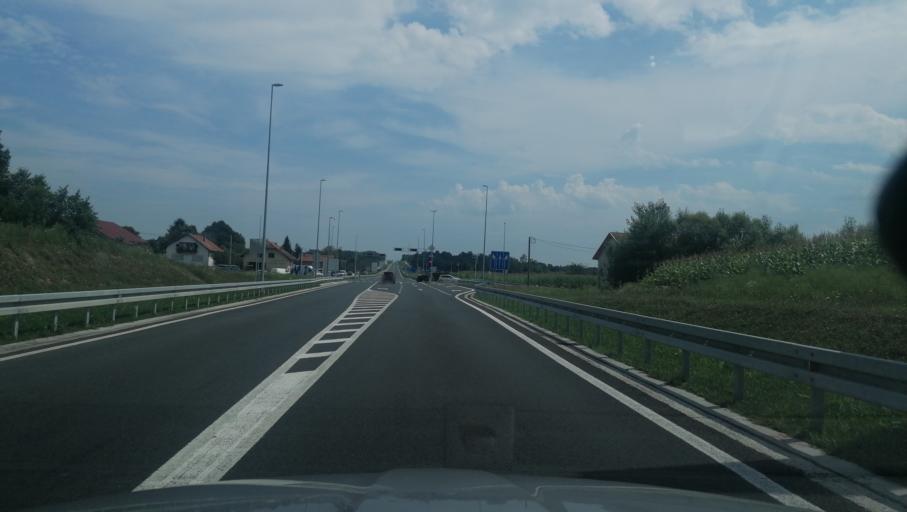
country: BA
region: Brcko
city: Brcko
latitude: 44.8355
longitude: 18.7844
